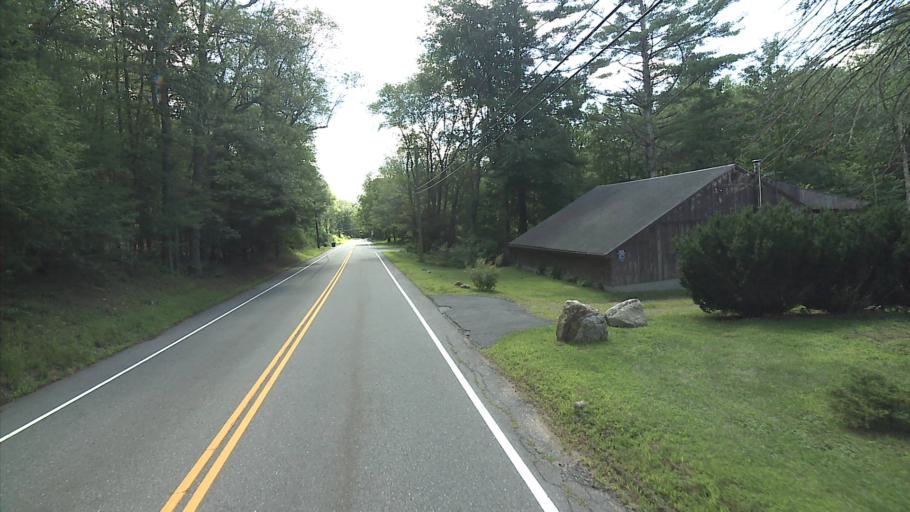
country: US
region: Connecticut
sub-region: Windham County
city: South Woodstock
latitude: 41.9559
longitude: -72.0778
